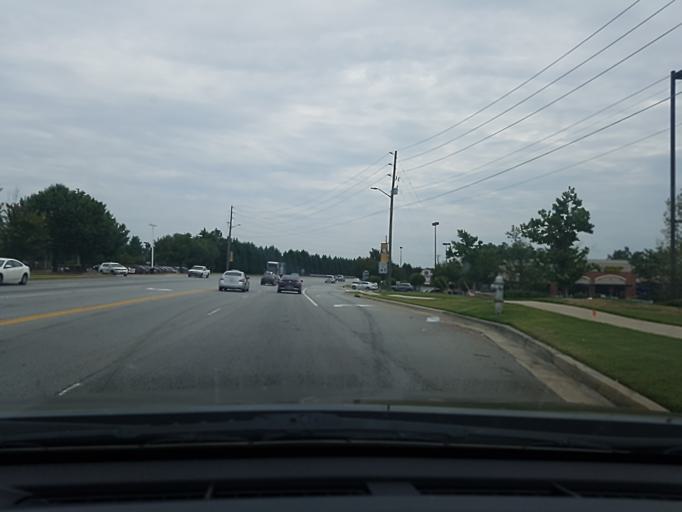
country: US
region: Georgia
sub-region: Gwinnett County
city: Duluth
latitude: 33.9624
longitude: -84.1420
